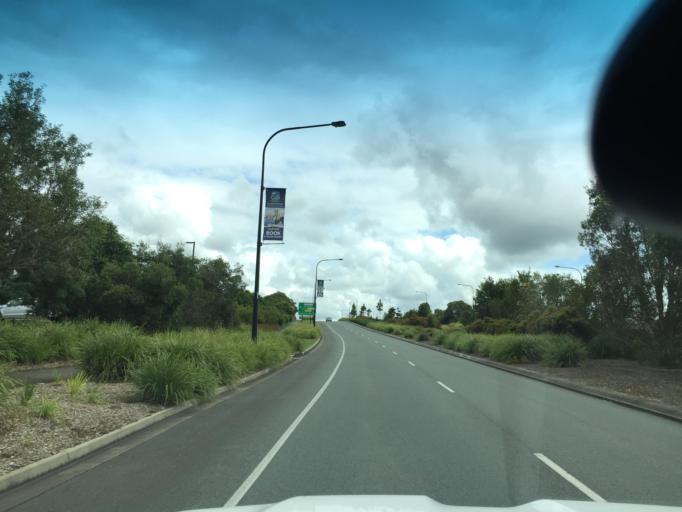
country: AU
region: Queensland
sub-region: Moreton Bay
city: Deception Bay
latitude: -27.2122
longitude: 152.9991
